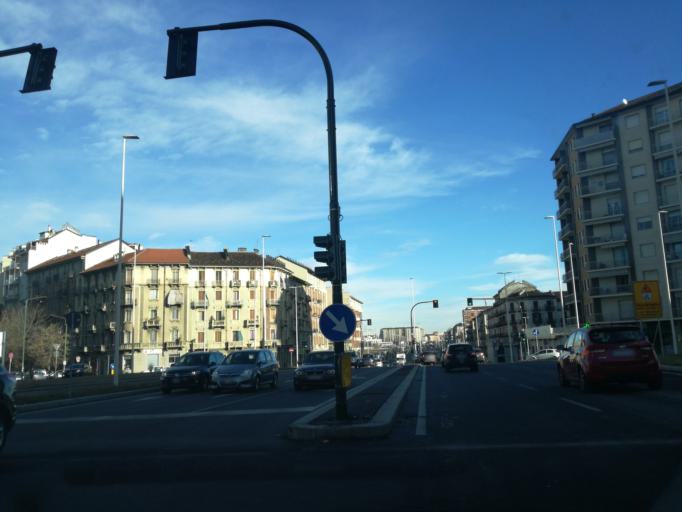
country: IT
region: Piedmont
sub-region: Provincia di Torino
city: Turin
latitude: 45.0805
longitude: 7.6712
